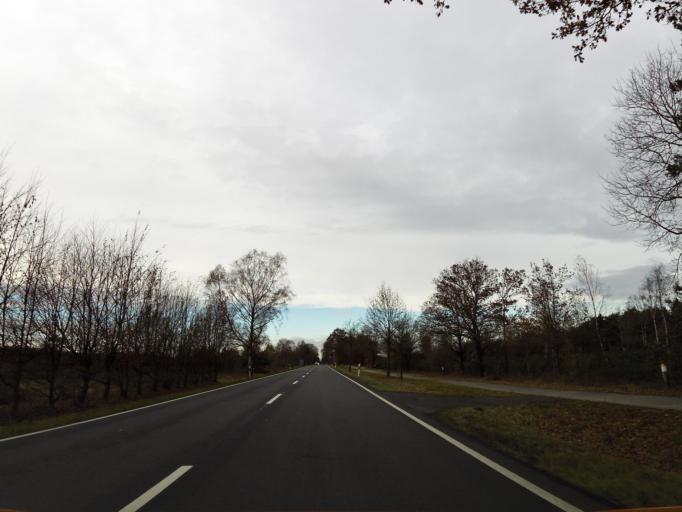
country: DE
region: Lower Saxony
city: Eimke
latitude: 52.9675
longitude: 10.2828
